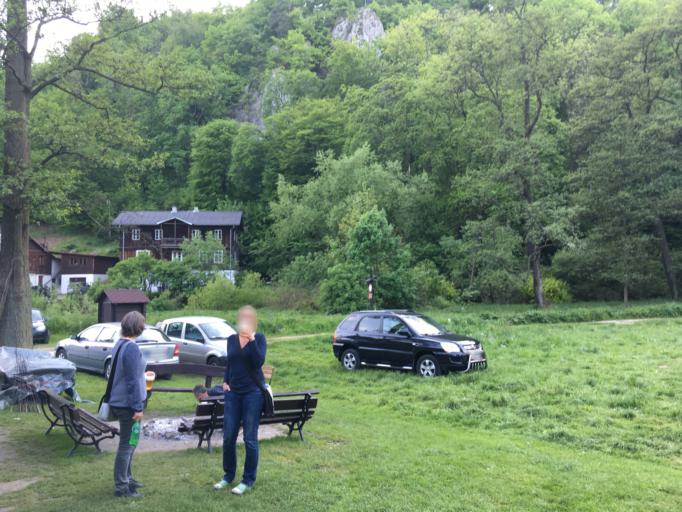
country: PL
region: Lesser Poland Voivodeship
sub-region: Powiat krakowski
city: Skala
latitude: 50.2084
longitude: 19.8289
